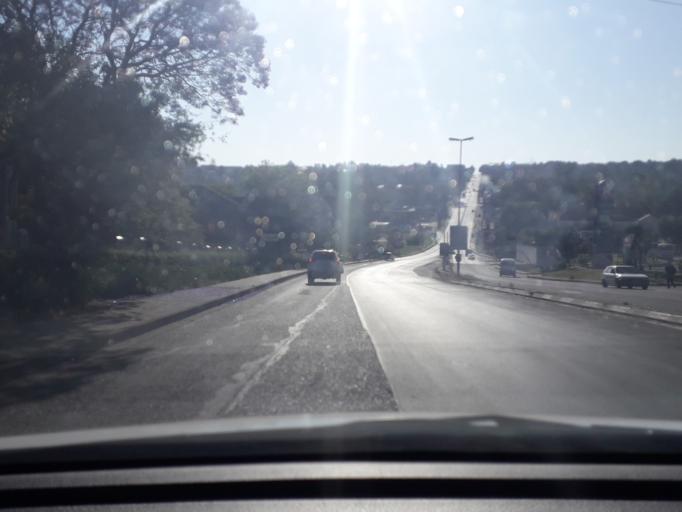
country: ZA
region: Gauteng
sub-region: City of Johannesburg Metropolitan Municipality
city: Johannesburg
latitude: -26.0982
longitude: 27.9887
